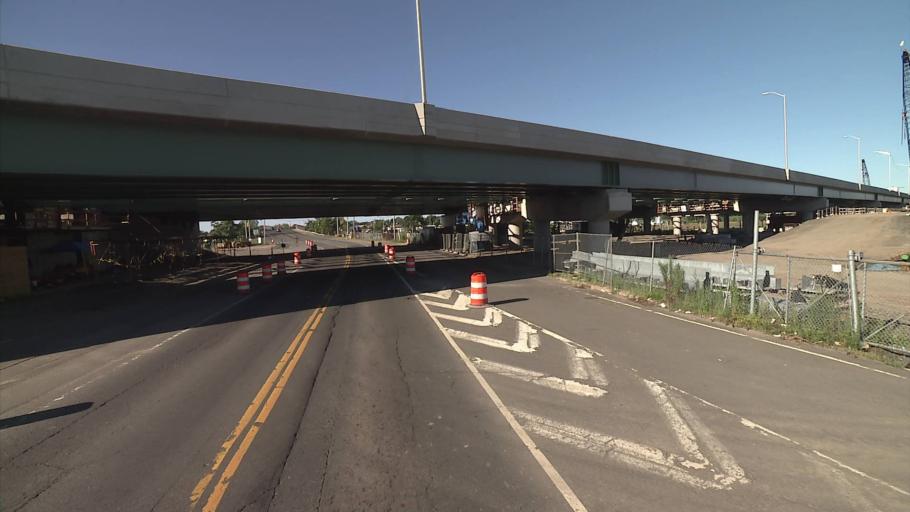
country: US
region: Connecticut
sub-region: New Haven County
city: West Haven
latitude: 41.2840
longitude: -72.9376
